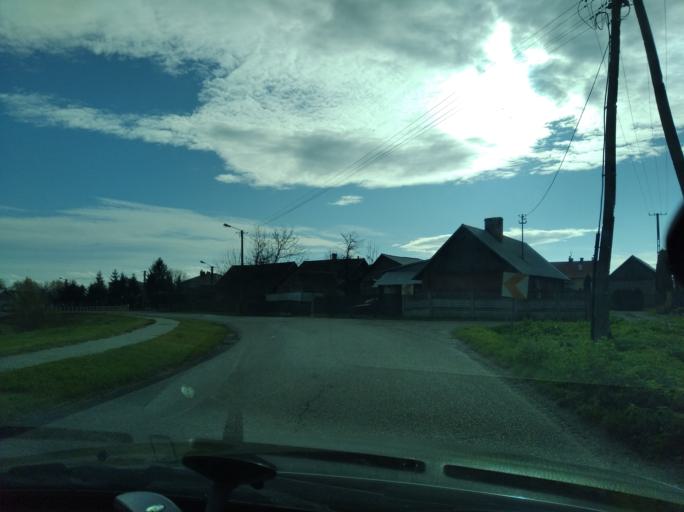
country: PL
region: Subcarpathian Voivodeship
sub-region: Powiat ropczycko-sedziszowski
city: Ostrow
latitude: 50.0932
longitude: 21.5546
